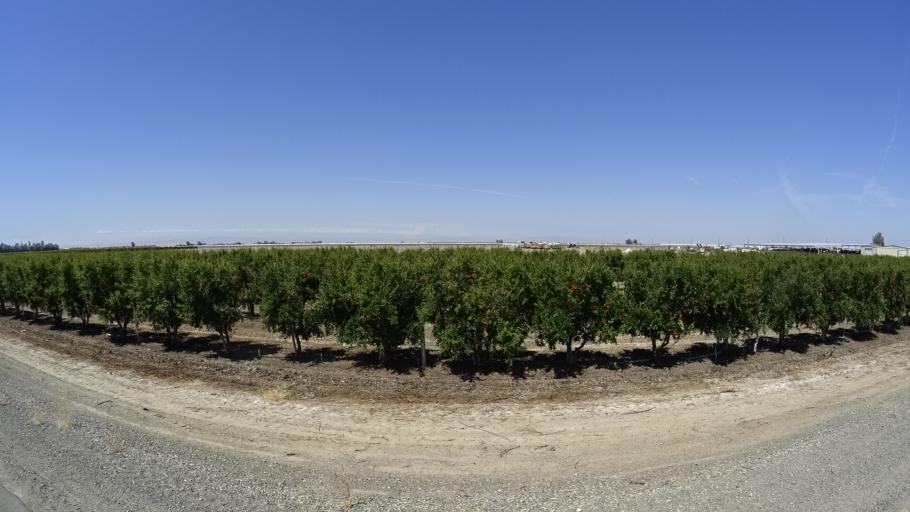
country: US
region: California
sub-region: Kings County
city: Stratford
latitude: 36.2222
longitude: -119.7982
